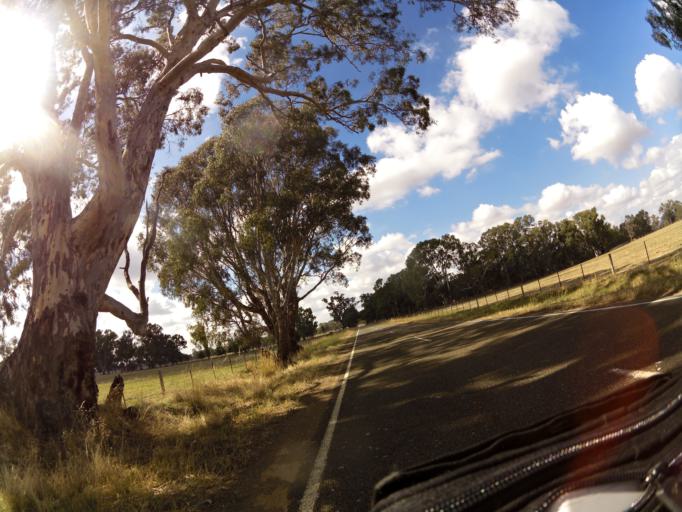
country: AU
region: Victoria
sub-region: Benalla
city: Benalla
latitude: -36.6130
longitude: 146.0236
